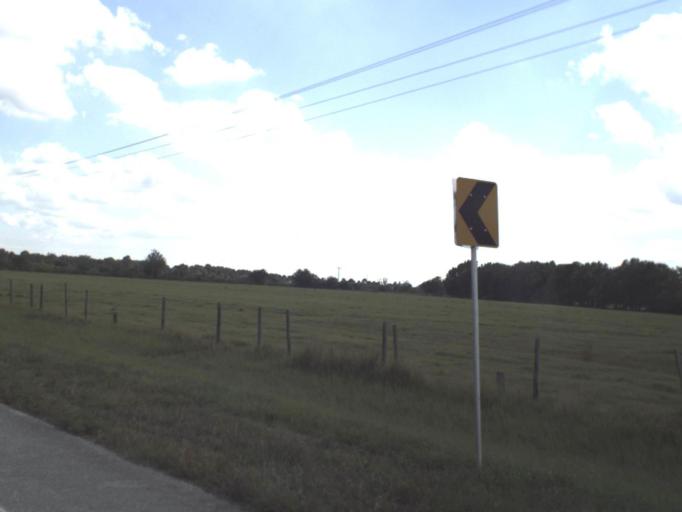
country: US
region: Florida
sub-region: Highlands County
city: Lake Placid
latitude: 27.4382
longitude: -81.2426
